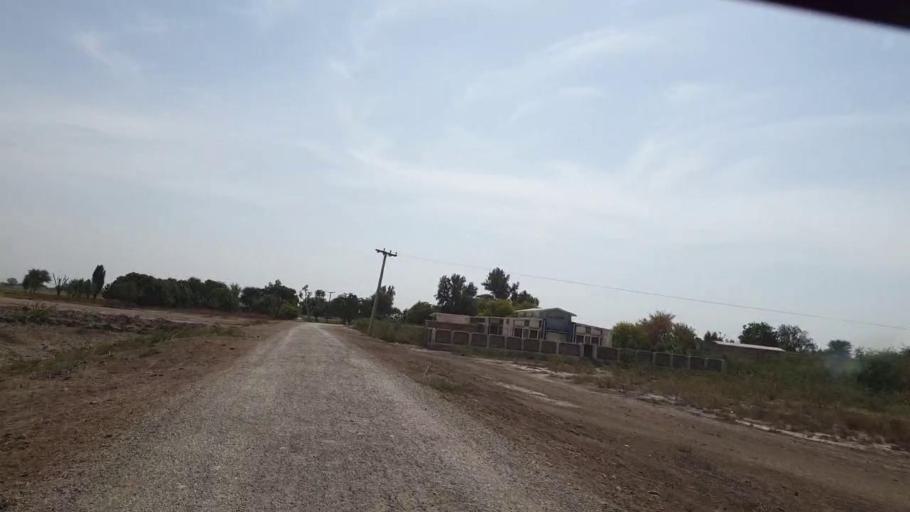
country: PK
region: Sindh
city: Kunri
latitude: 25.1533
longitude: 69.5455
